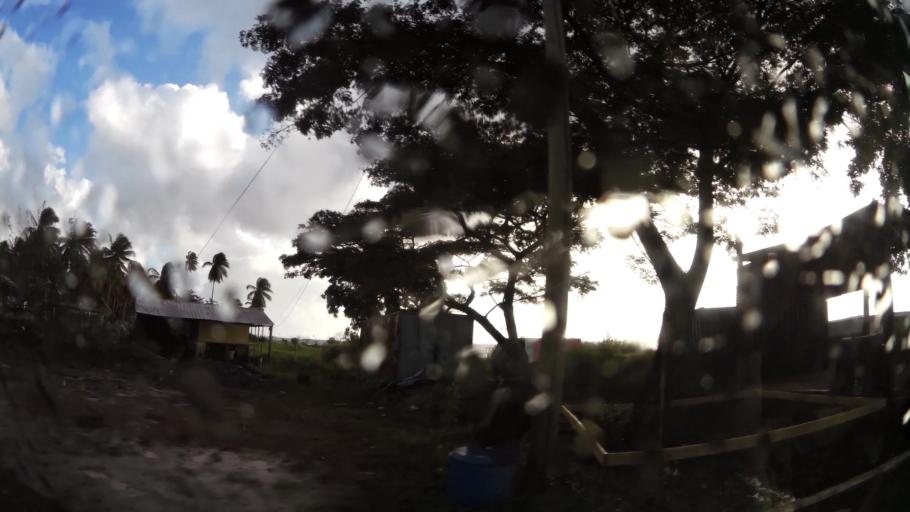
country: DM
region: Saint Paul
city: Mahaut
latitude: 15.3686
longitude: -61.4041
